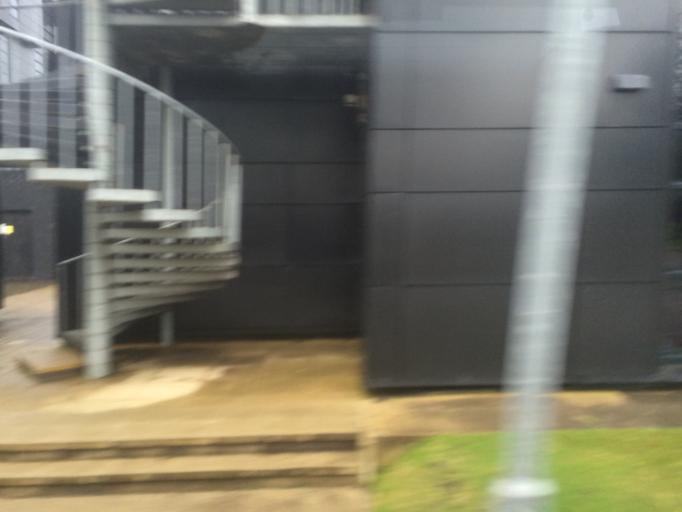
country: GB
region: Scotland
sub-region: North Lanarkshire
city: Holytown
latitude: 55.8351
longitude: -3.9836
